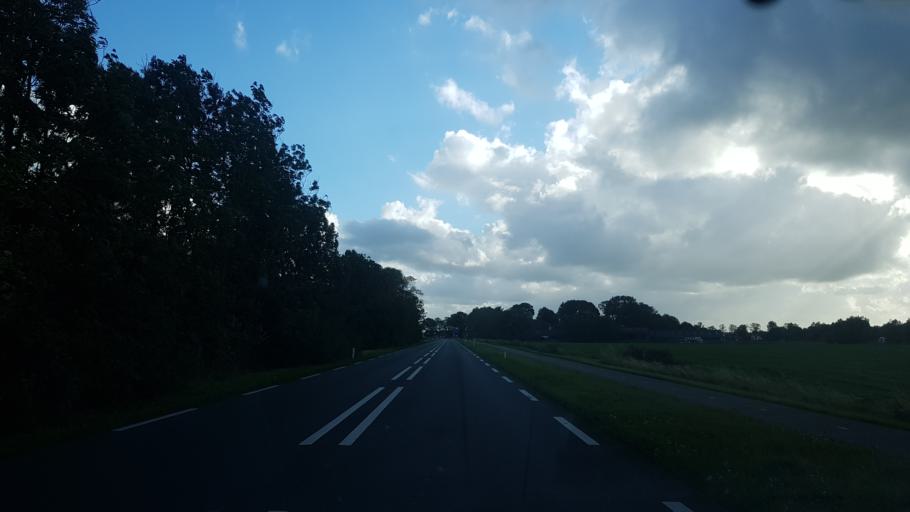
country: NL
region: Groningen
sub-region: Gemeente Slochteren
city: Slochteren
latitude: 53.3037
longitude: 6.7351
